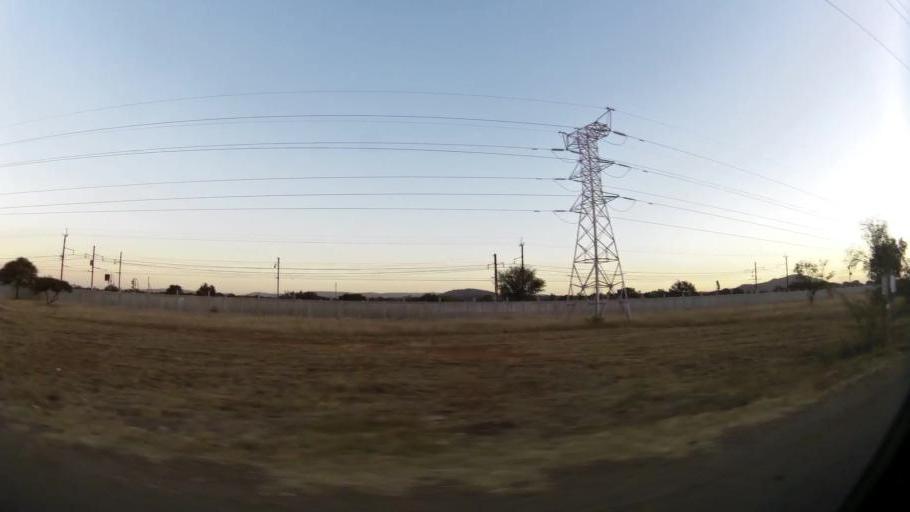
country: ZA
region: North-West
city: Ga-Rankuwa
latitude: -25.6204
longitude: 28.0077
